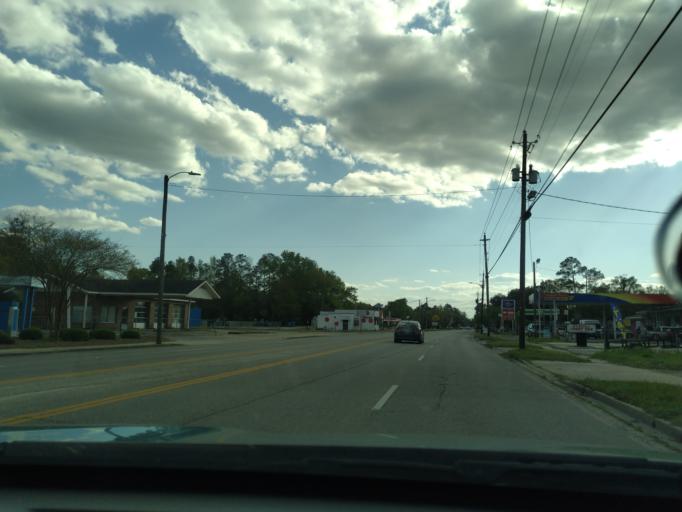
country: US
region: South Carolina
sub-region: Williamsburg County
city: Kingstree
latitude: 33.6815
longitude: -79.8261
